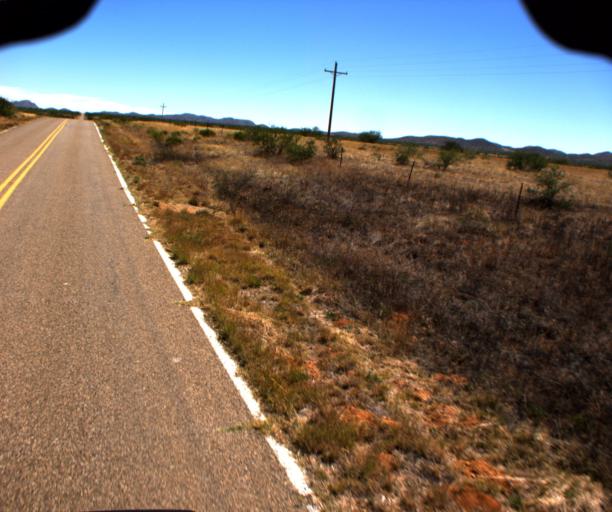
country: US
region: Arizona
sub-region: Pima County
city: Sells
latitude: 31.5503
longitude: -111.5397
